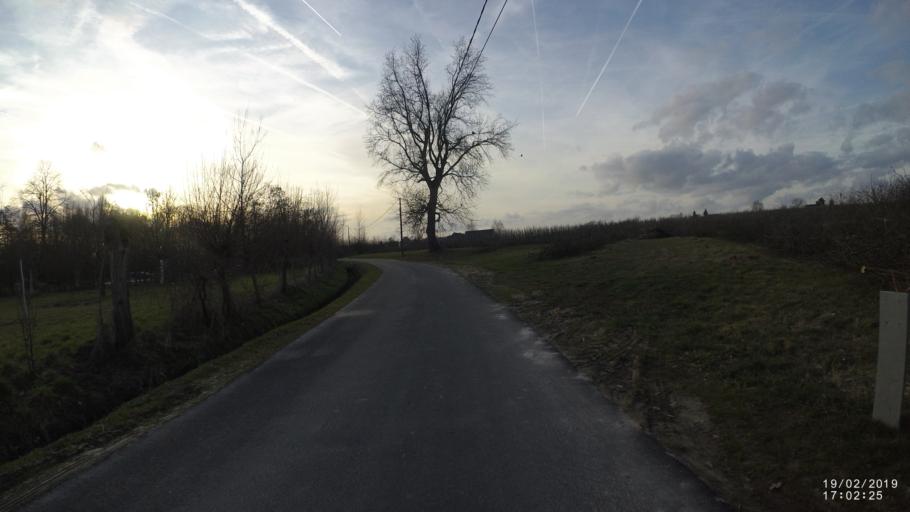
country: BE
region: Flanders
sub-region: Provincie Limburg
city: Borgloon
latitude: 50.8127
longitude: 5.3043
